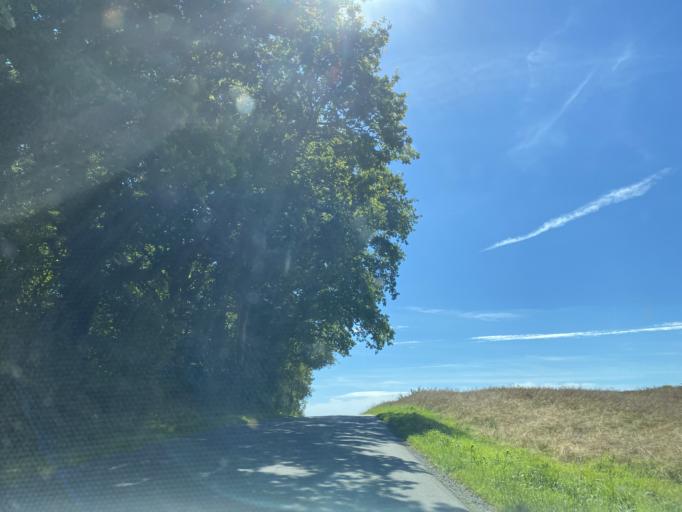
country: DK
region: South Denmark
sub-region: Kolding Kommune
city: Christiansfeld
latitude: 55.3856
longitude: 9.5136
